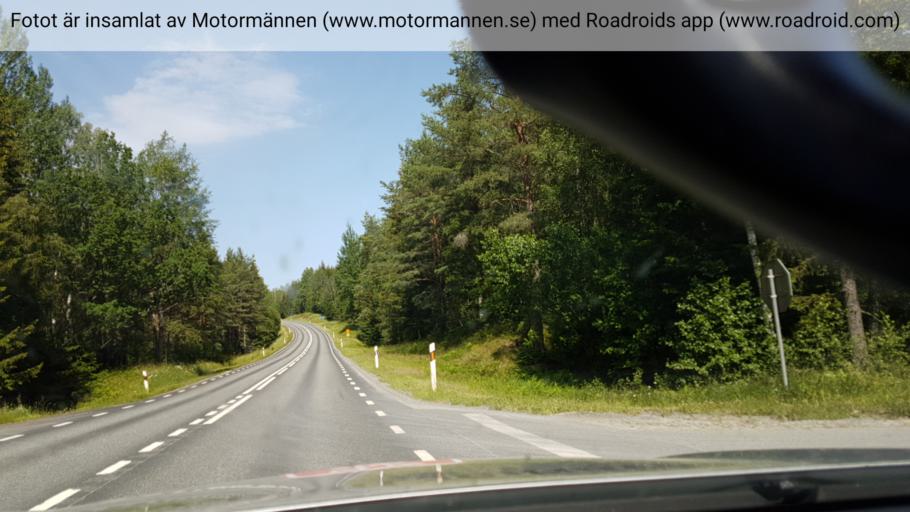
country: SE
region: Joenkoeping
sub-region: Aneby Kommun
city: Aneby
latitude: 57.8732
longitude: 14.8715
